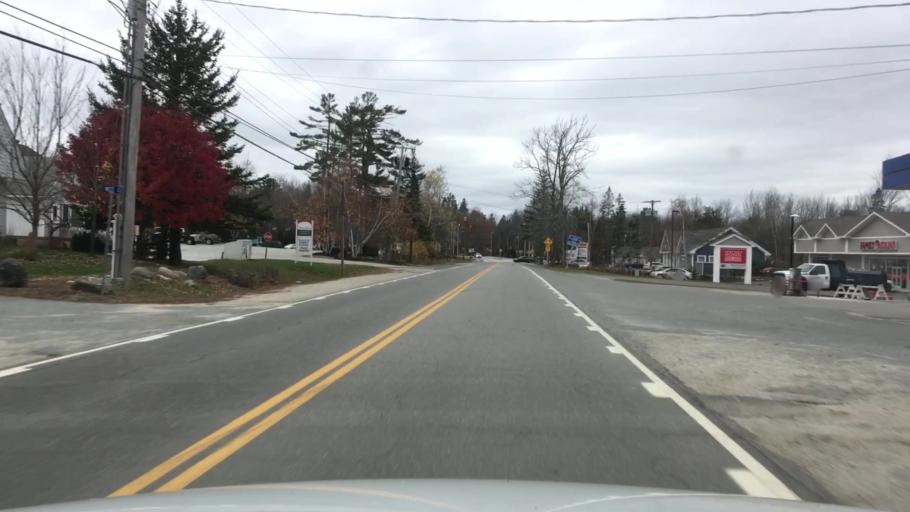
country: US
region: Maine
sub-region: Hancock County
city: Sedgwick
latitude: 44.4061
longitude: -68.5951
